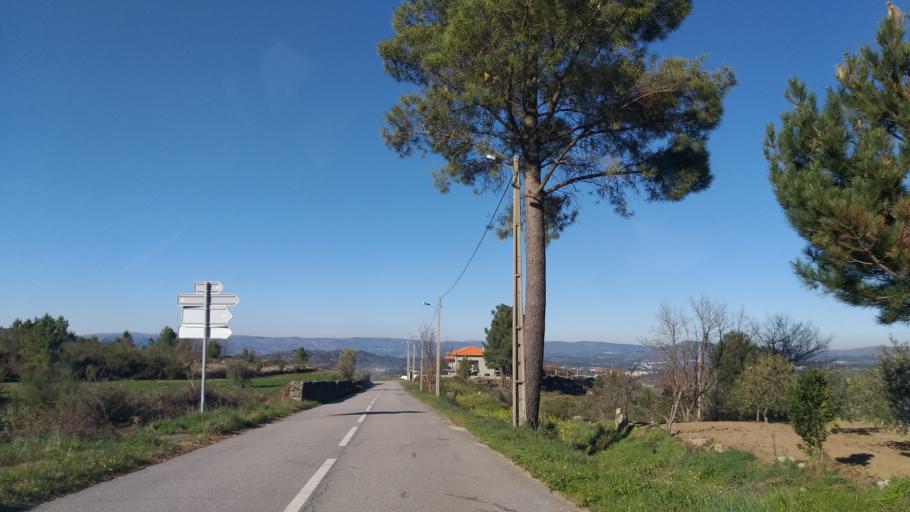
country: PT
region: Guarda
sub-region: Celorico da Beira
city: Celorico da Beira
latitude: 40.5905
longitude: -7.3584
